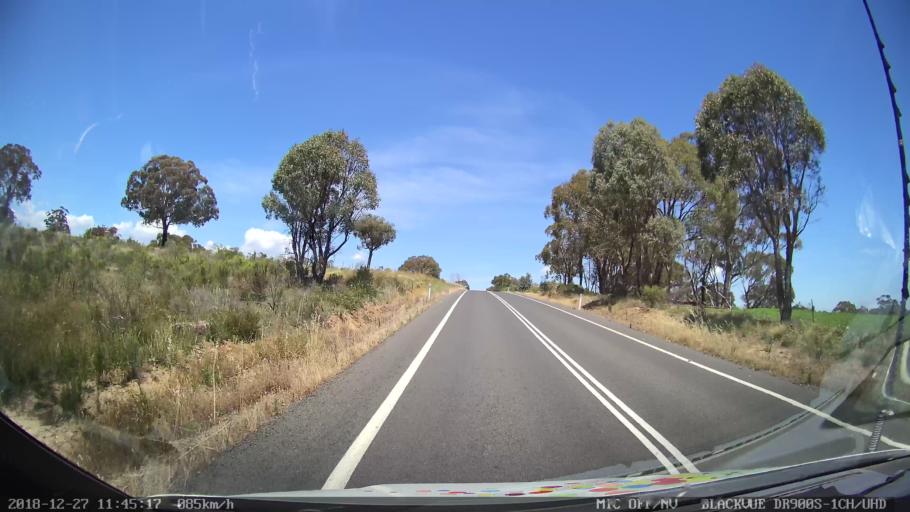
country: AU
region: New South Wales
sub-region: Bathurst Regional
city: Perthville
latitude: -33.5810
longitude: 149.4715
